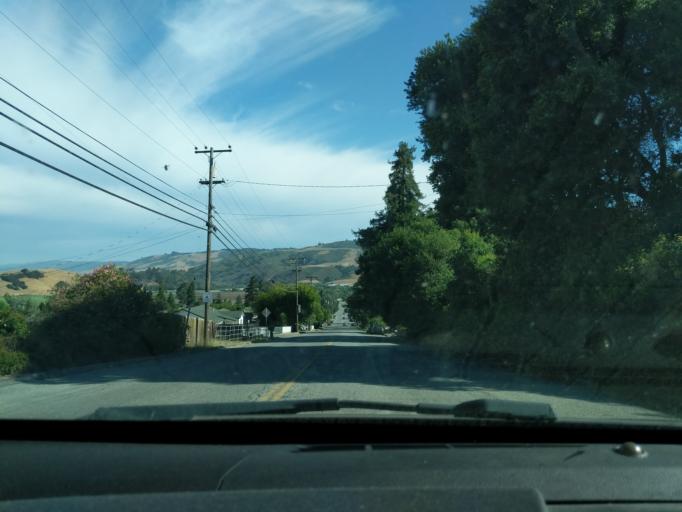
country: US
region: California
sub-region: San Benito County
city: Aromas
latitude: 36.8844
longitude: -121.6424
